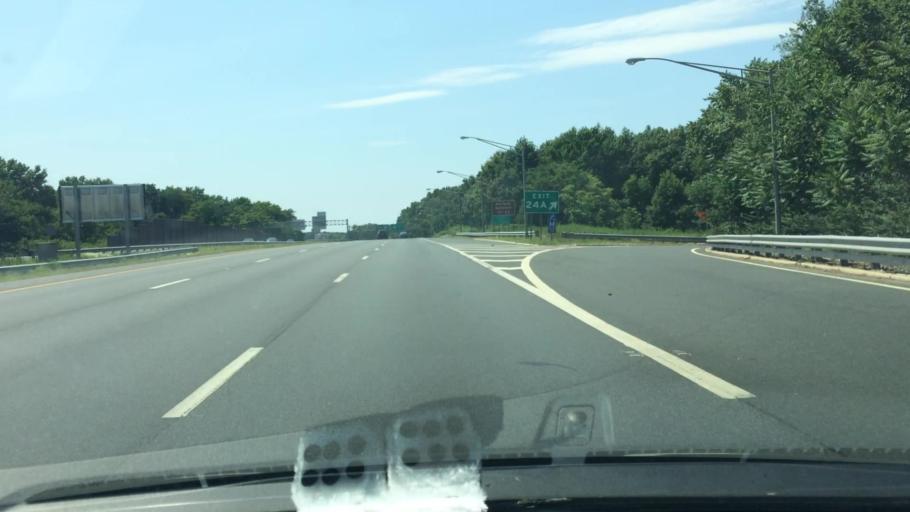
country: US
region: New Jersey
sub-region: Gloucester County
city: Westville
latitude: 39.8602
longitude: -75.1373
